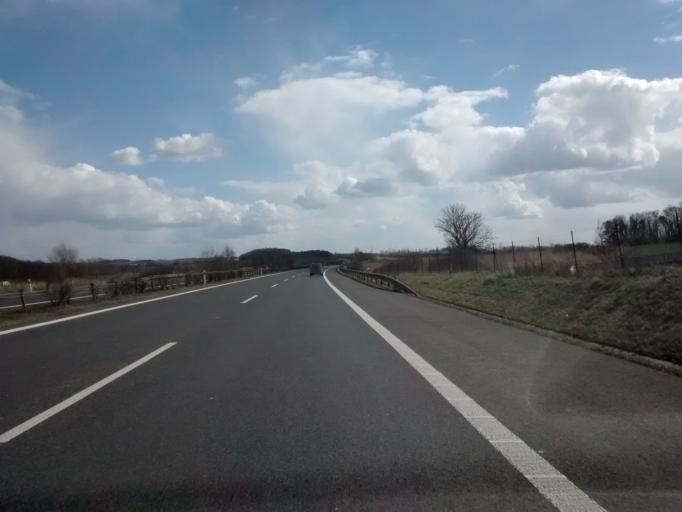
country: CZ
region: Ustecky
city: Roudnice nad Labem
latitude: 50.3821
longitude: 14.2438
